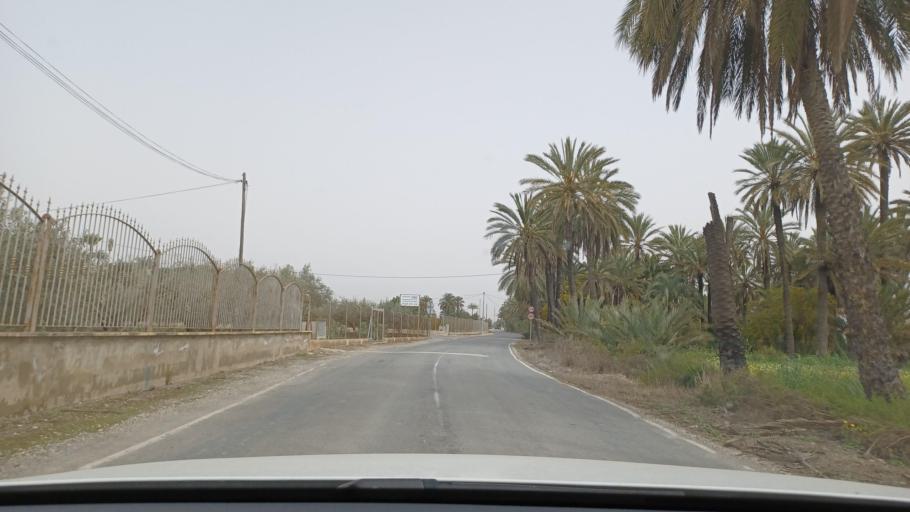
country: ES
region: Valencia
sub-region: Provincia de Alicante
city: Elche
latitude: 38.2228
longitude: -0.6953
